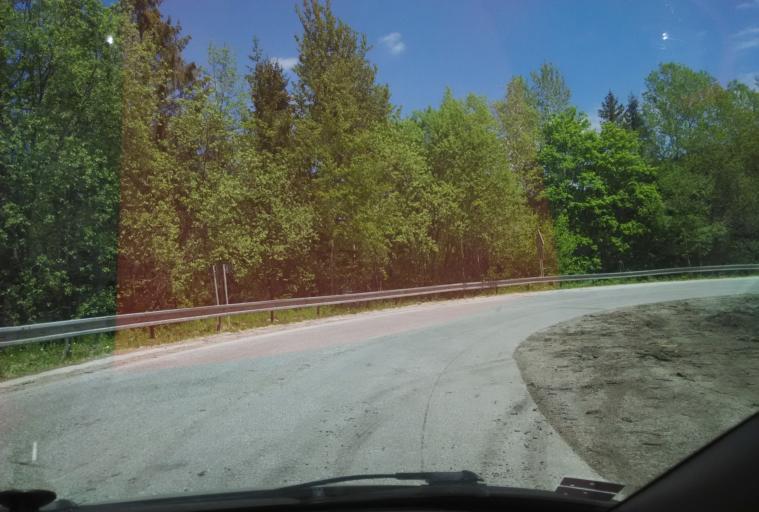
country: SK
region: Kosicky
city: Dobsina
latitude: 48.8568
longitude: 20.3791
